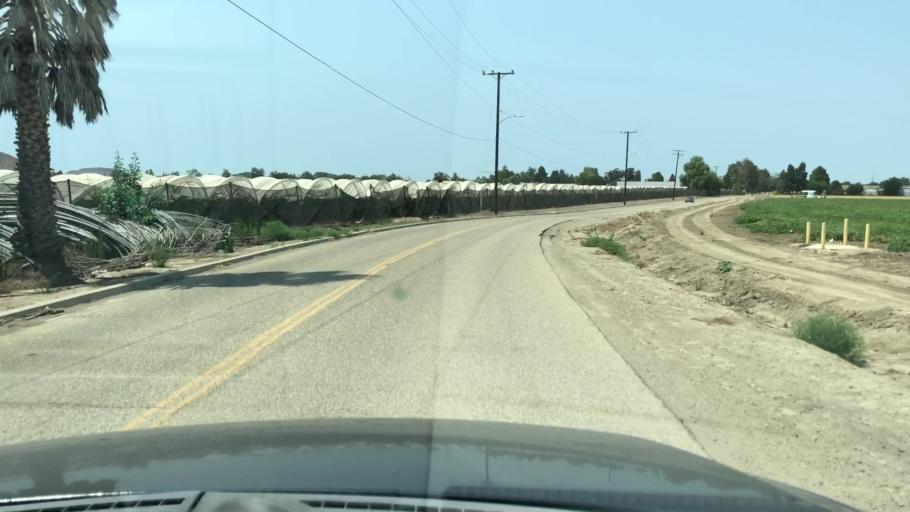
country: US
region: California
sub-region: Ventura County
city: Camarillo
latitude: 34.2053
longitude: -119.0005
